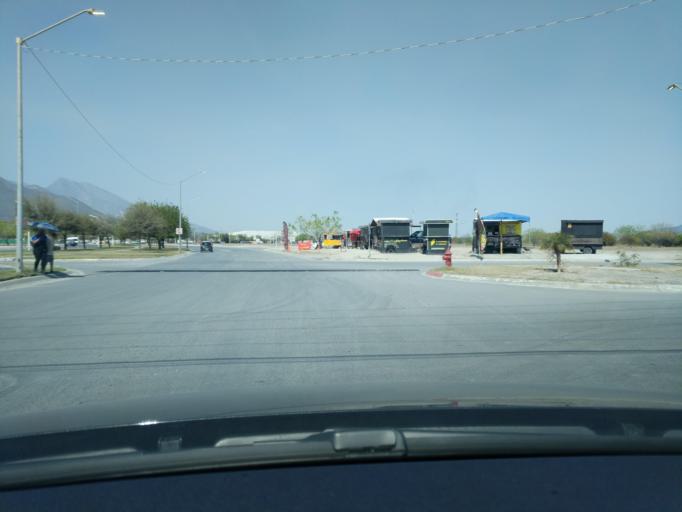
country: MX
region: Nuevo Leon
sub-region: Garcia
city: Los Parques
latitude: 25.7839
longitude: -100.4856
